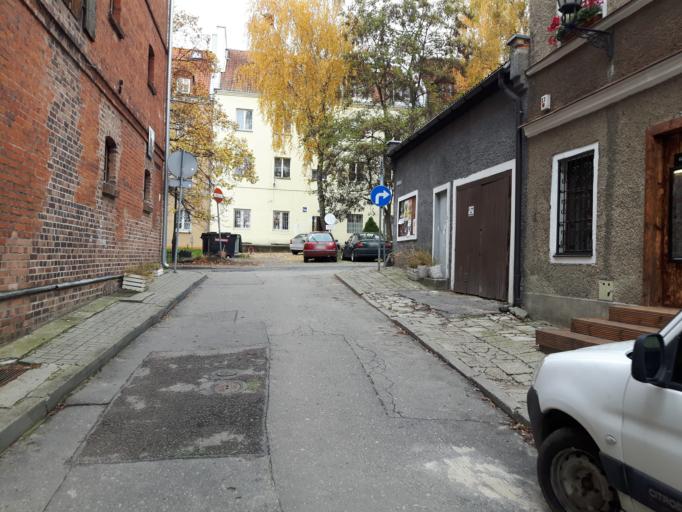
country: PL
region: Warmian-Masurian Voivodeship
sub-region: Powiat olsztynski
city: Olsztyn
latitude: 53.7755
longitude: 20.4765
